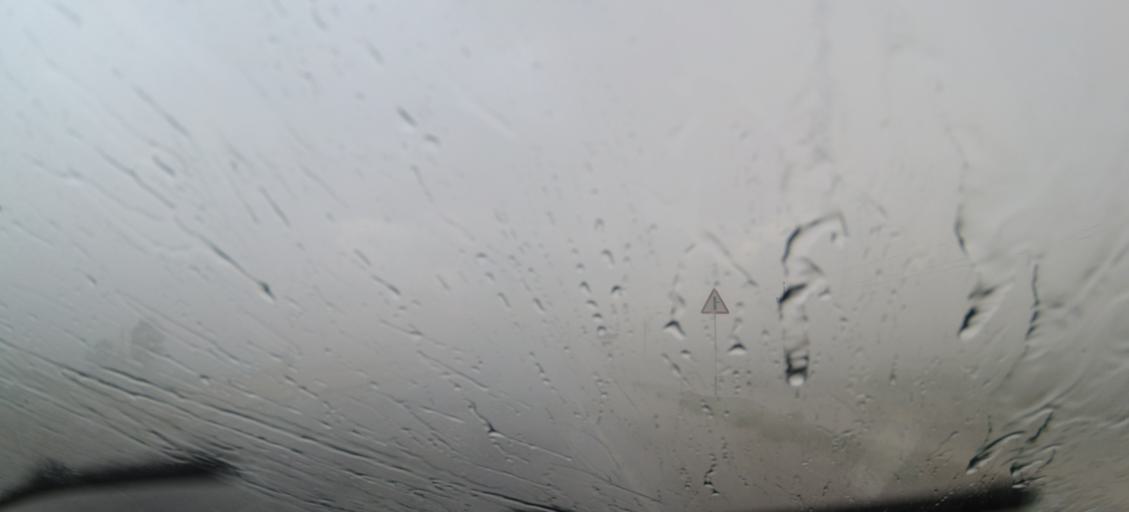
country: RU
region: Rostov
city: Proletarsk
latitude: 46.6895
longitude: 41.7347
